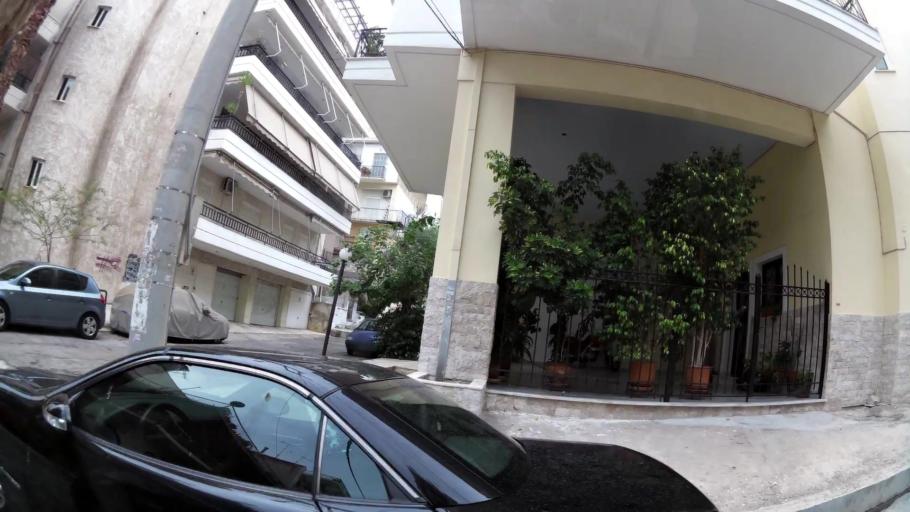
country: GR
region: Attica
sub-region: Nomos Attikis
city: Piraeus
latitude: 37.9343
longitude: 23.6303
